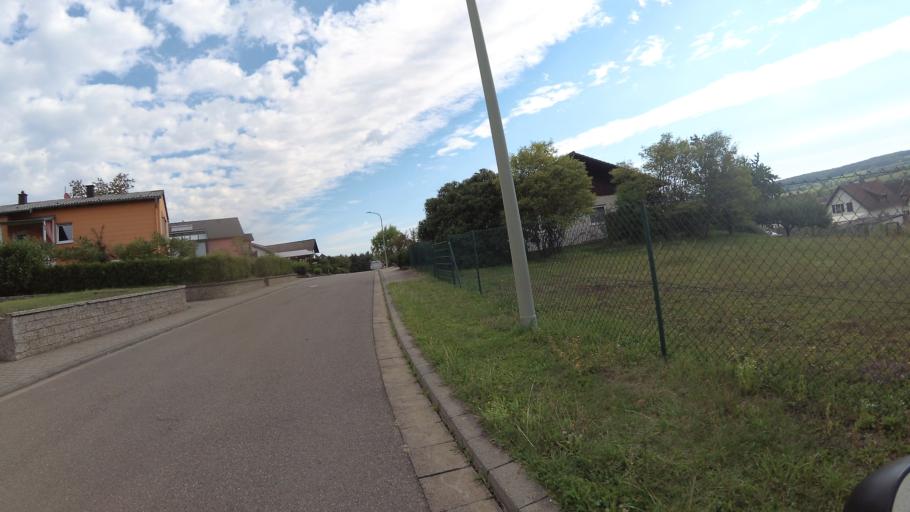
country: DE
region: Saarland
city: Gersheim
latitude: 49.1400
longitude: 7.1833
